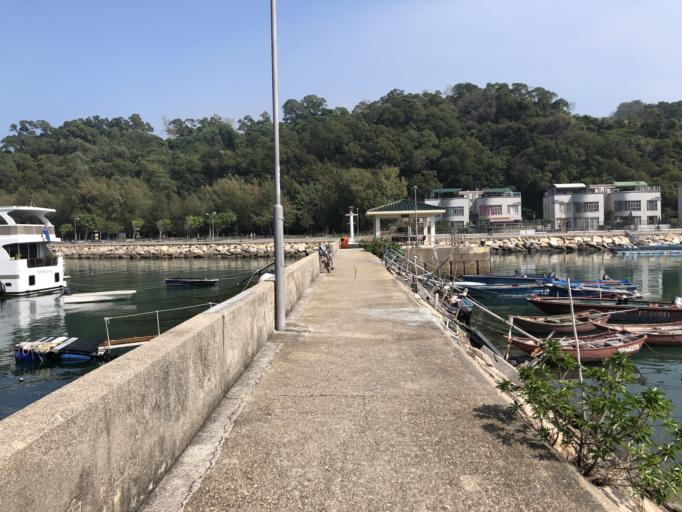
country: HK
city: Yung Shue Wan
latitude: 22.2013
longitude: 114.0203
